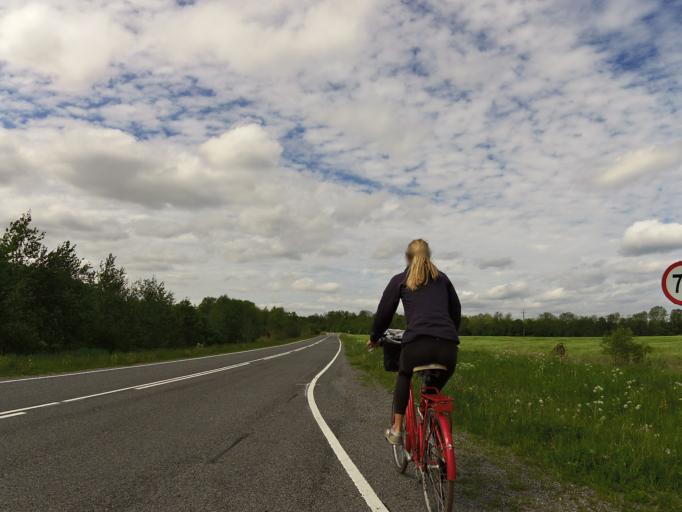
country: EE
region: Harju
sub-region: Paldiski linn
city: Paldiski
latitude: 59.2497
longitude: 23.8714
